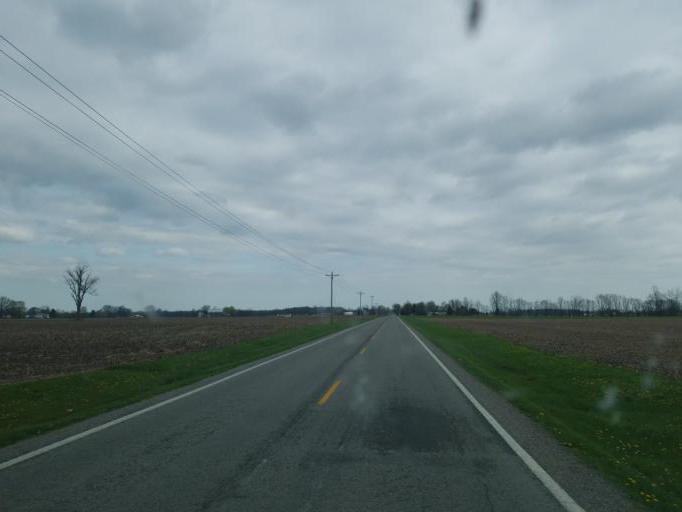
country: US
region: Ohio
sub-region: Morrow County
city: Cardington
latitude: 40.5940
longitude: -82.9623
